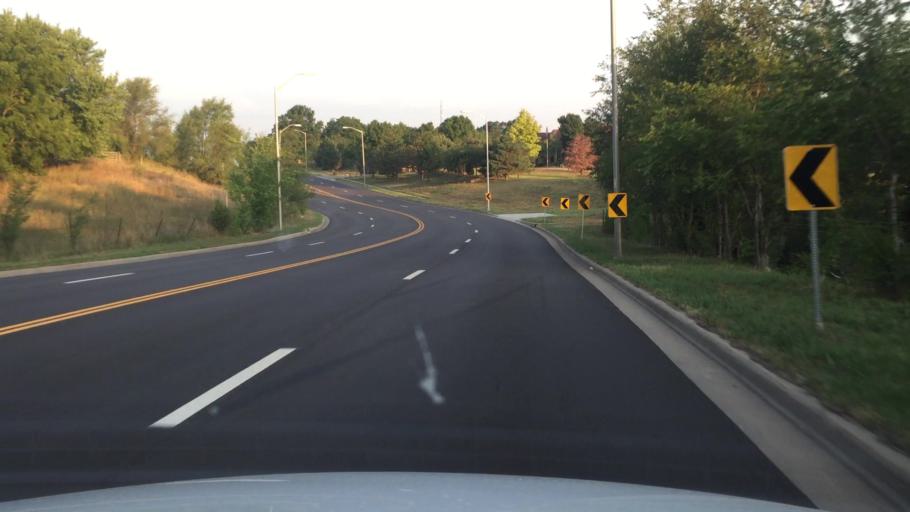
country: US
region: Kansas
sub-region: Johnson County
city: Shawnee
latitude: 39.0223
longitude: -94.7722
